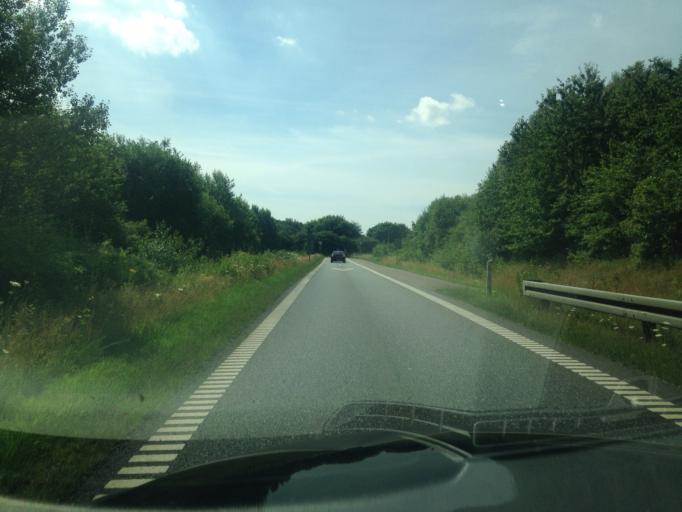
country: DK
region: South Denmark
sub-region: Kolding Kommune
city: Kolding
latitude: 55.5329
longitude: 9.4971
